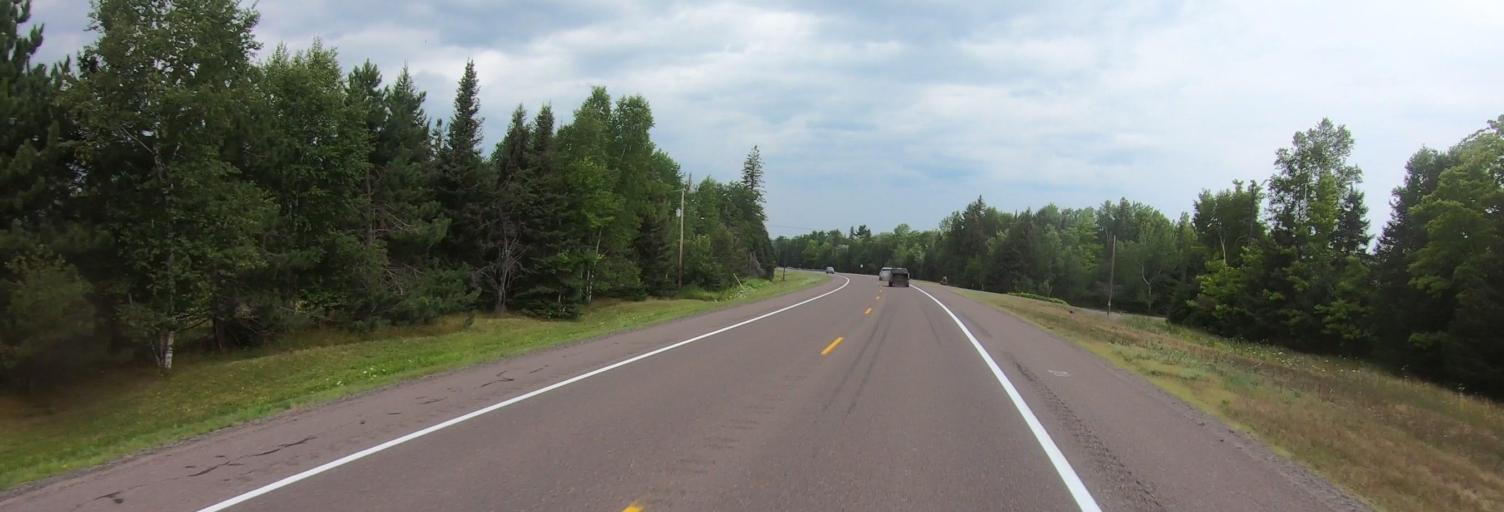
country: US
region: Michigan
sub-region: Baraga County
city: Baraga
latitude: 46.8739
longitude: -88.4761
